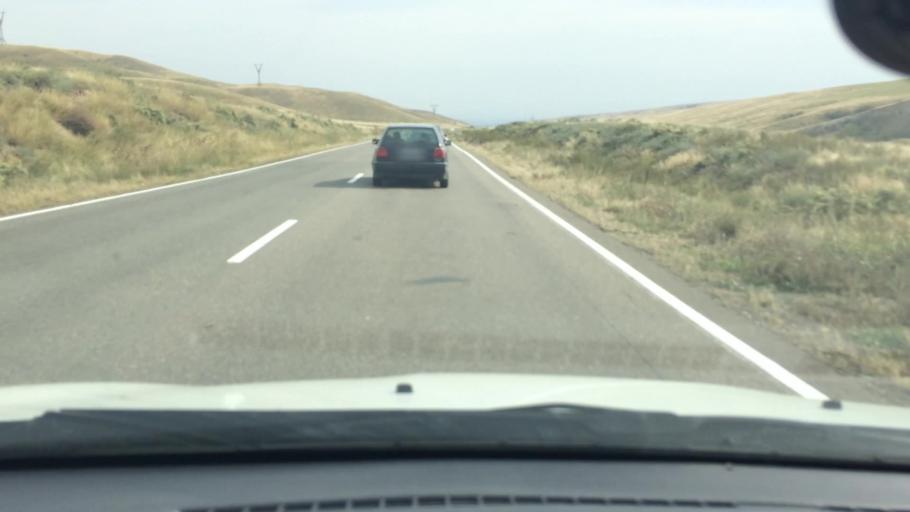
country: GE
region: Kvemo Kartli
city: Rust'avi
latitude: 41.5180
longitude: 44.9428
